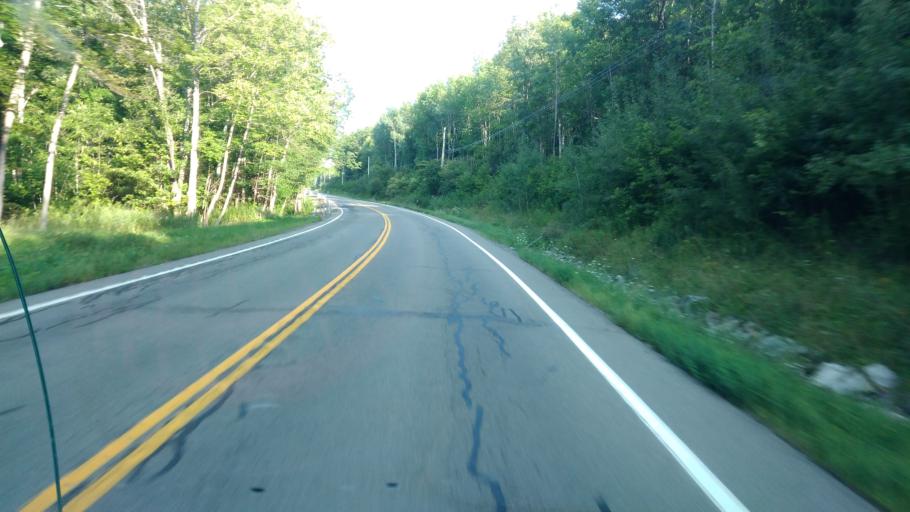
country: US
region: New York
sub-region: Allegany County
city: Andover
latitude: 42.1514
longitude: -77.6933
